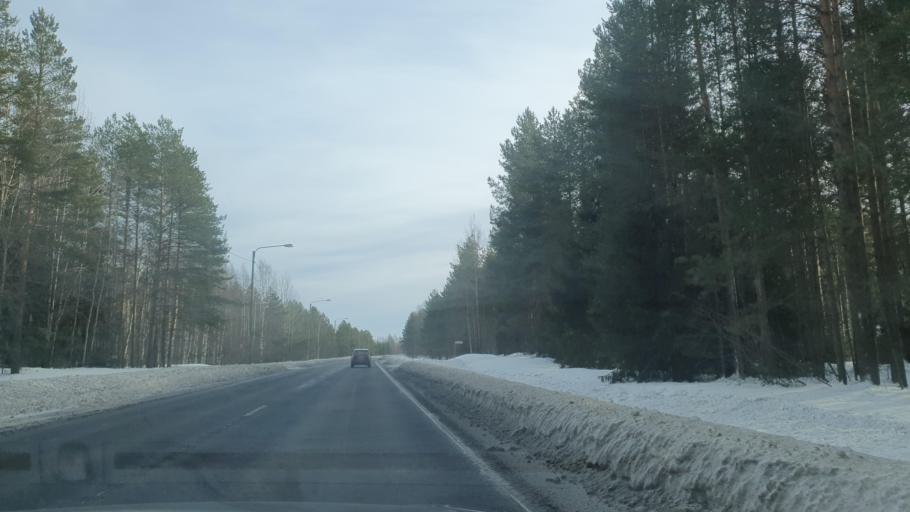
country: FI
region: Northern Ostrobothnia
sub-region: Oulu
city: Muhos
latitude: 64.8666
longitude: 25.8765
